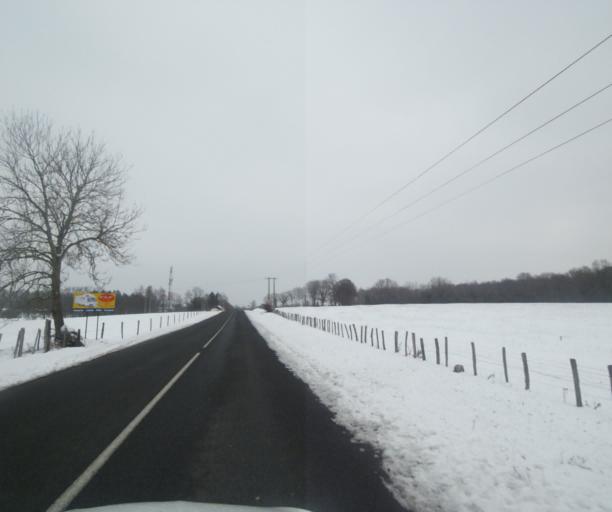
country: FR
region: Champagne-Ardenne
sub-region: Departement de la Haute-Marne
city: Villiers-en-Lieu
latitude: 48.6129
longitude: 4.8876
